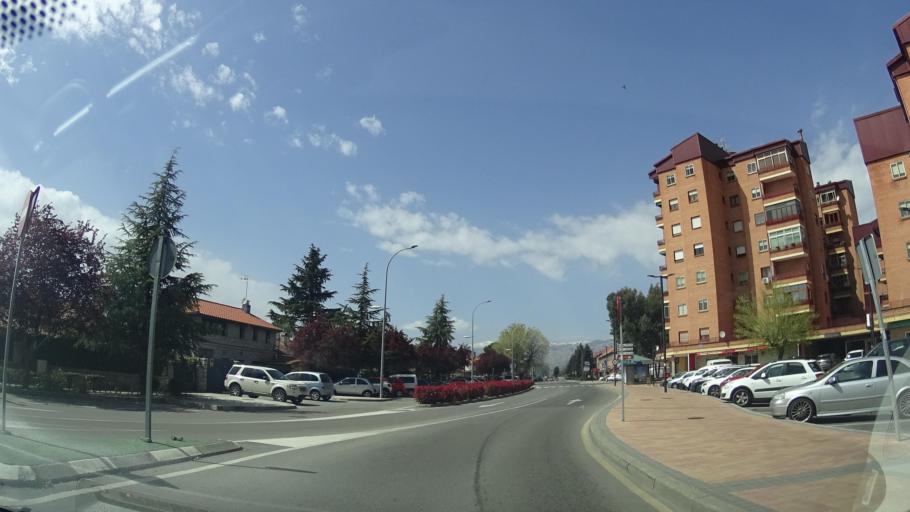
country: ES
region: Madrid
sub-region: Provincia de Madrid
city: Colmenar Viejo
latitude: 40.6698
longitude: -3.7730
